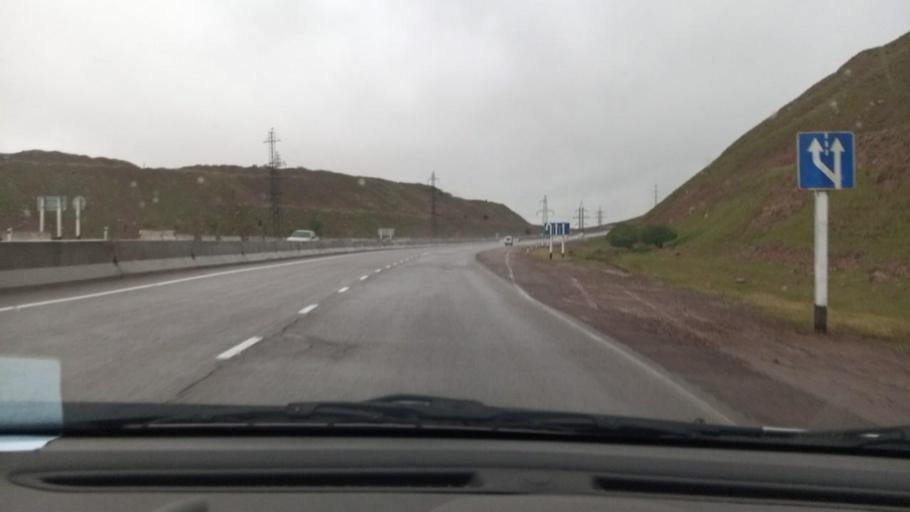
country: UZ
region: Toshkent
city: Angren
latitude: 41.0598
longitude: 70.1991
